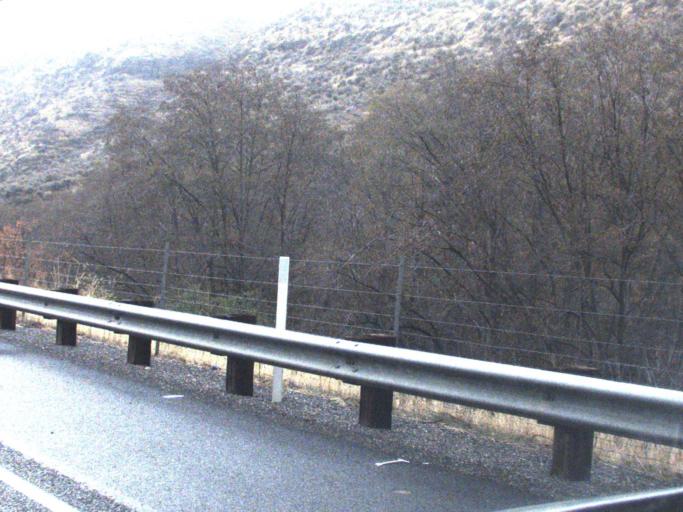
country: US
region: Washington
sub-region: Asotin County
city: Clarkston Heights-Vineland
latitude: 46.4085
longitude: -117.2644
